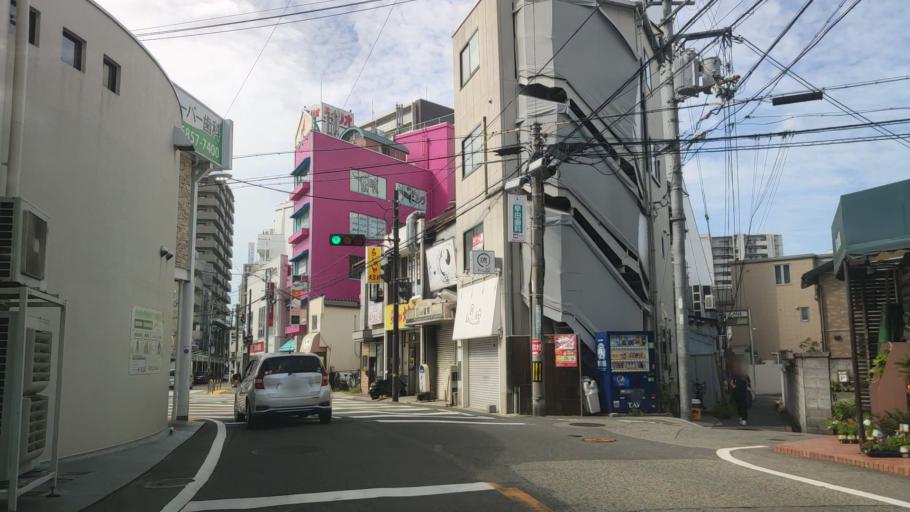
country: JP
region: Osaka
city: Toyonaka
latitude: 34.7891
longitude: 135.4637
